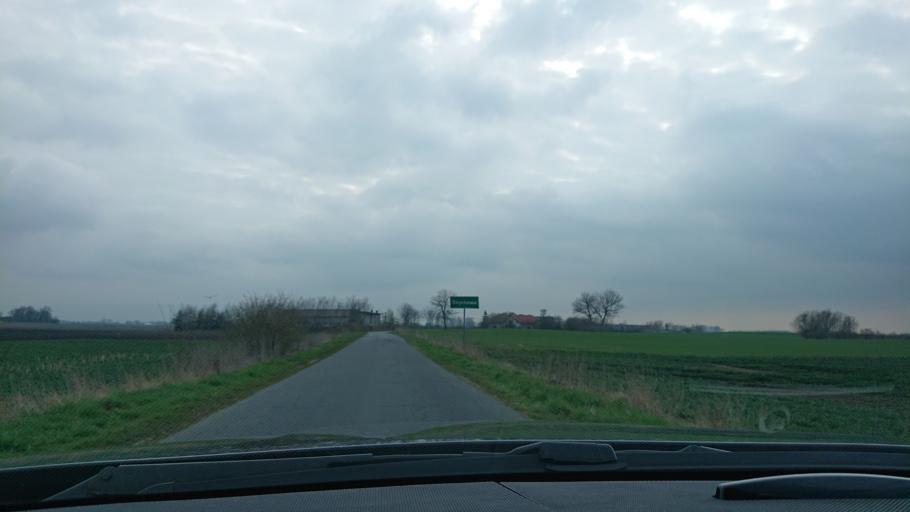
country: PL
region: Greater Poland Voivodeship
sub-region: Powiat gnieznienski
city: Gniezno
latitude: 52.5568
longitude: 17.5121
